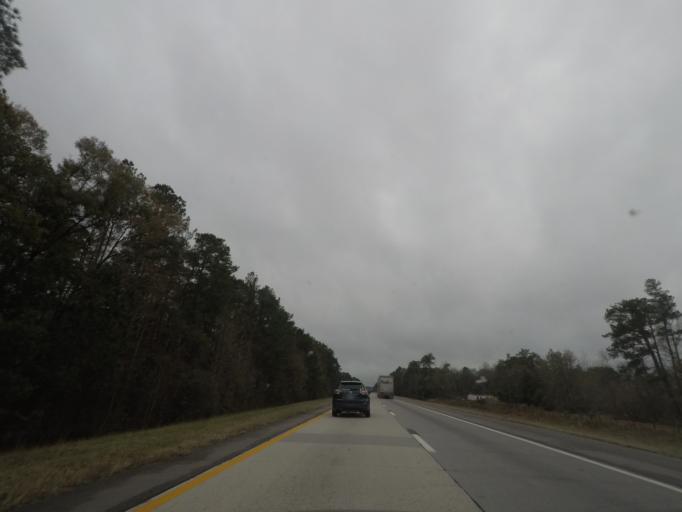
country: US
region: South Carolina
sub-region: Dorchester County
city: Saint George
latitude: 33.1128
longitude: -80.6434
